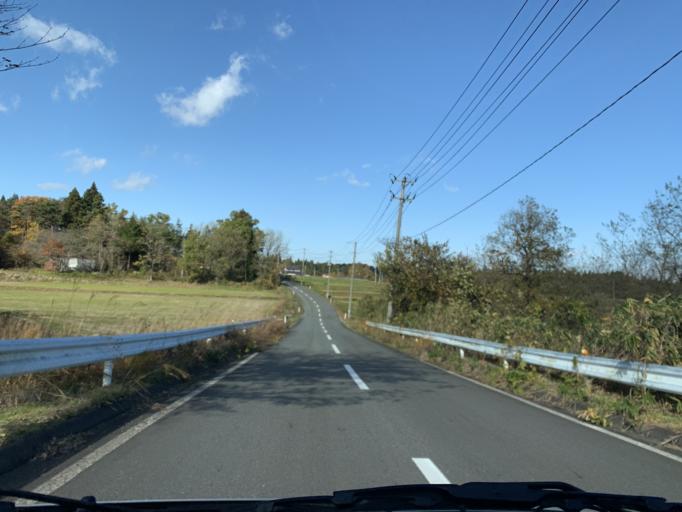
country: JP
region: Iwate
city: Mizusawa
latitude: 39.0645
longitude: 141.1126
